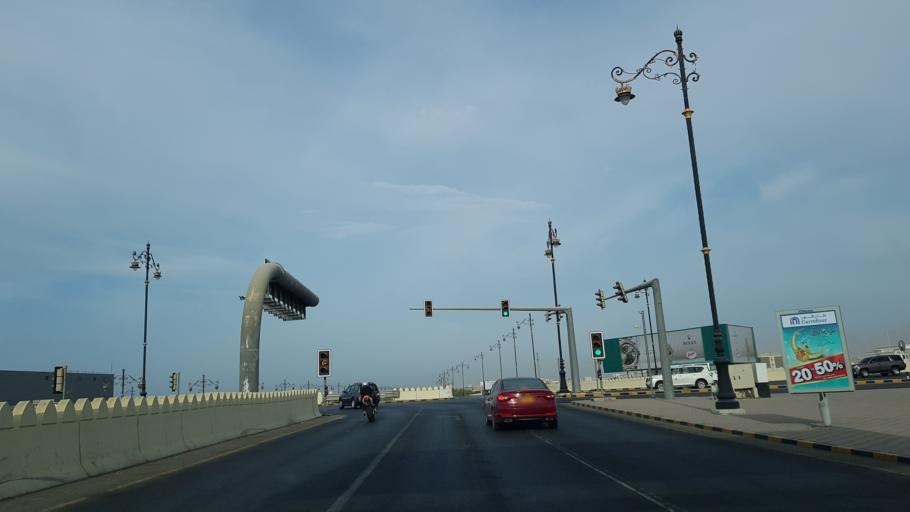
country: OM
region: Muhafazat Masqat
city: Bawshar
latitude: 23.5862
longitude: 58.2952
